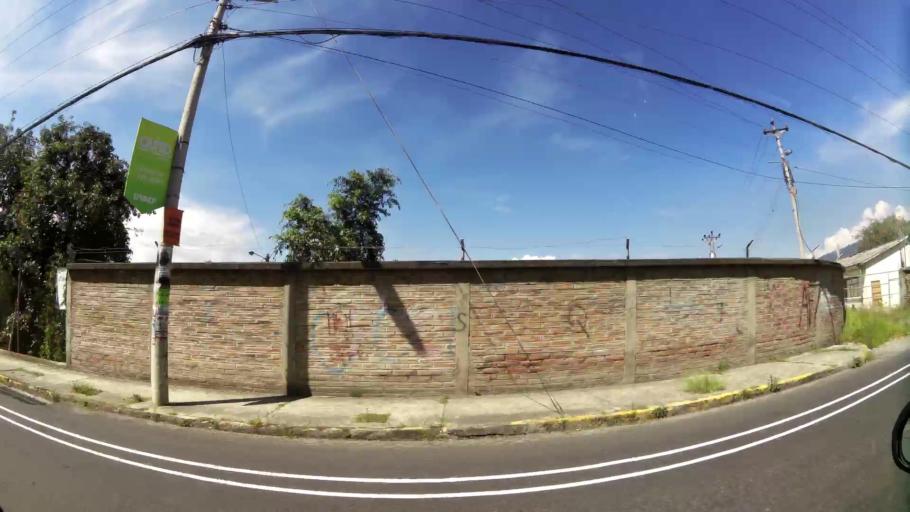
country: EC
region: Pichincha
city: Quito
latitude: -0.1969
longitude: -78.4292
